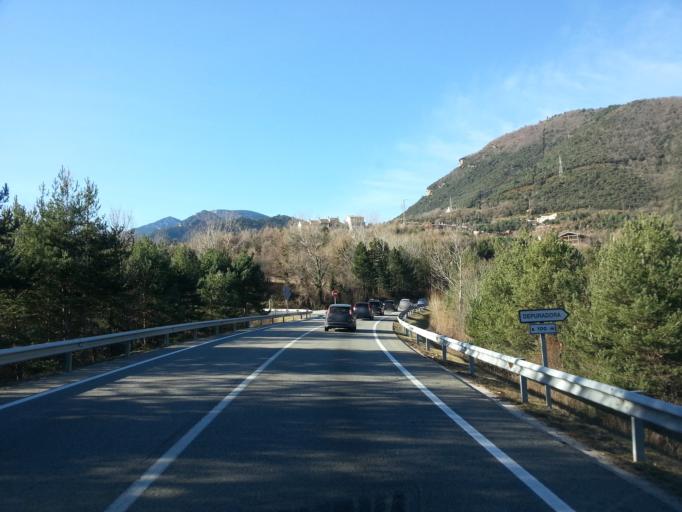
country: ES
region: Catalonia
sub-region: Provincia de Barcelona
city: Berga
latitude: 42.1521
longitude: 1.8618
